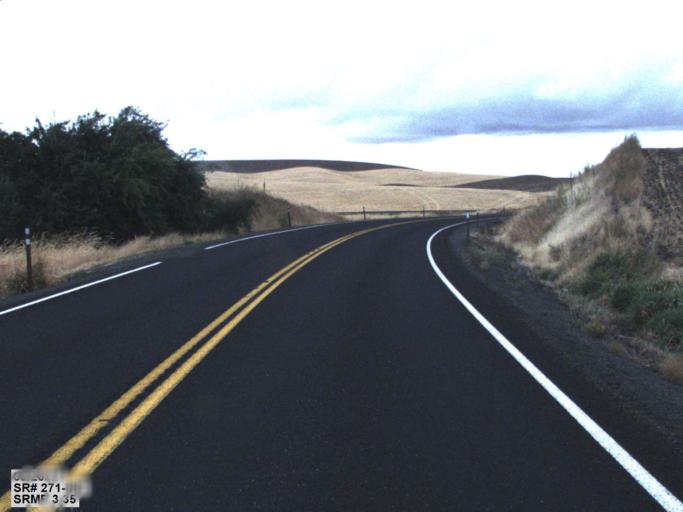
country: US
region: Washington
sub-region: Whitman County
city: Colfax
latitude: 47.1676
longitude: -117.2887
